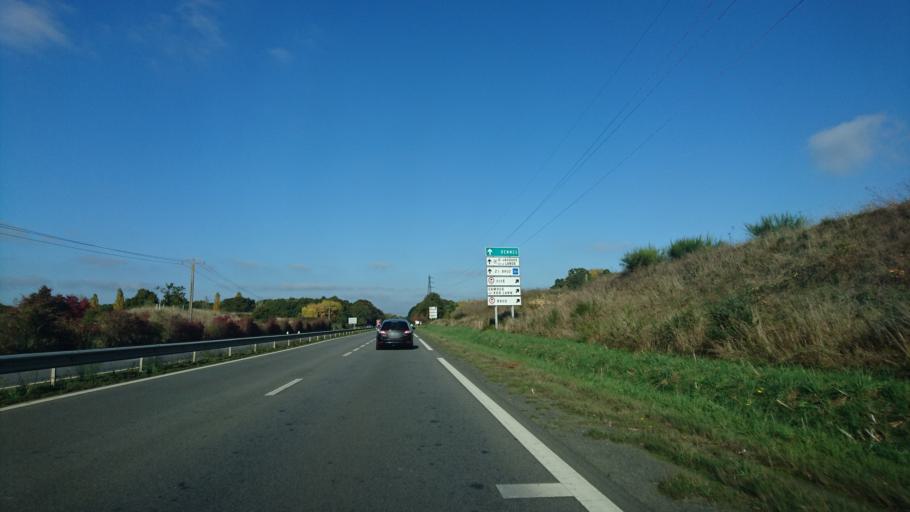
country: FR
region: Brittany
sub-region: Departement d'Ille-et-Vilaine
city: Bruz
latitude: 48.0375
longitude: -1.7575
